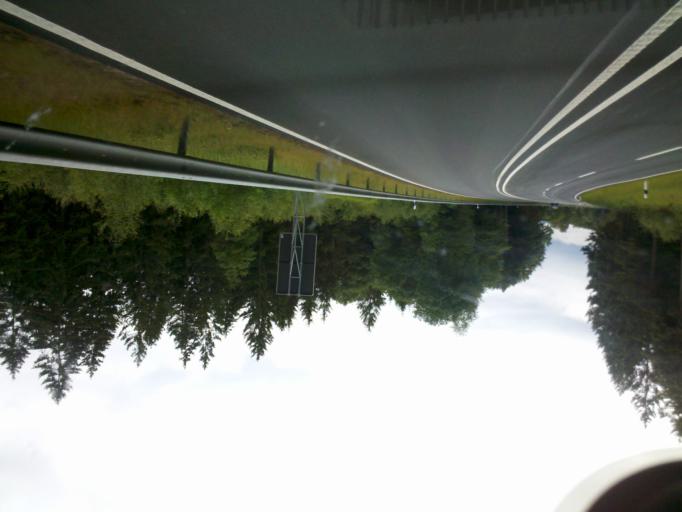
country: DE
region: North Rhine-Westphalia
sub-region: Regierungsbezirk Arnsberg
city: Olpe
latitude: 51.0536
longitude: 7.9011
